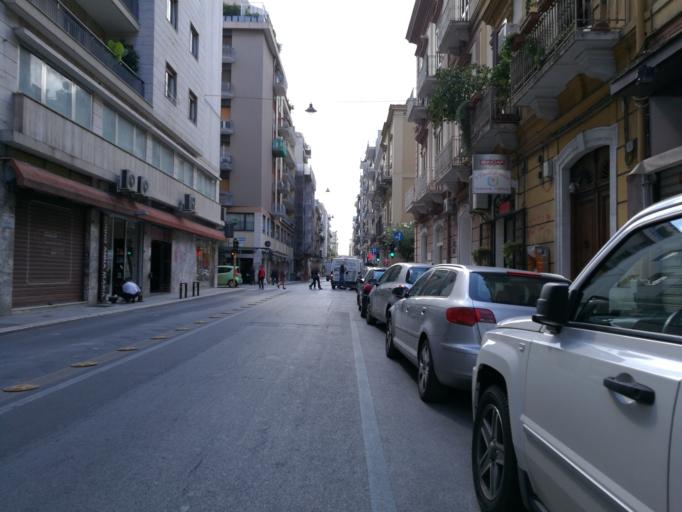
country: IT
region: Apulia
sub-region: Provincia di Bari
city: Bari
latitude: 41.1237
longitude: 16.8687
